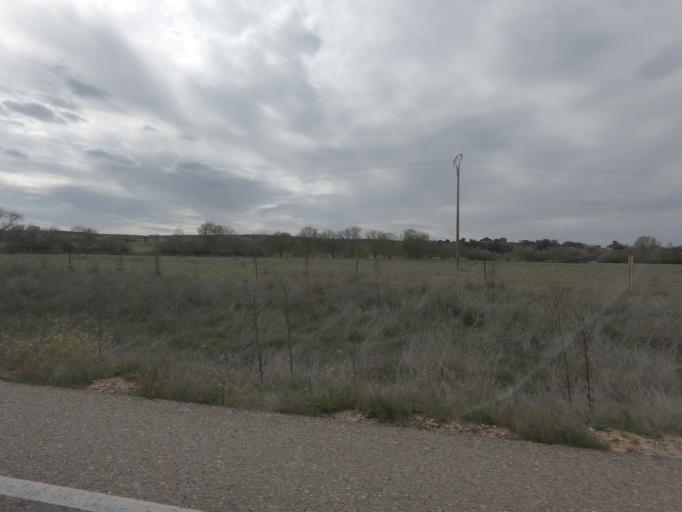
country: ES
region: Castille and Leon
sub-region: Provincia de Salamanca
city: Pastores
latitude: 40.5429
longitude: -6.5633
